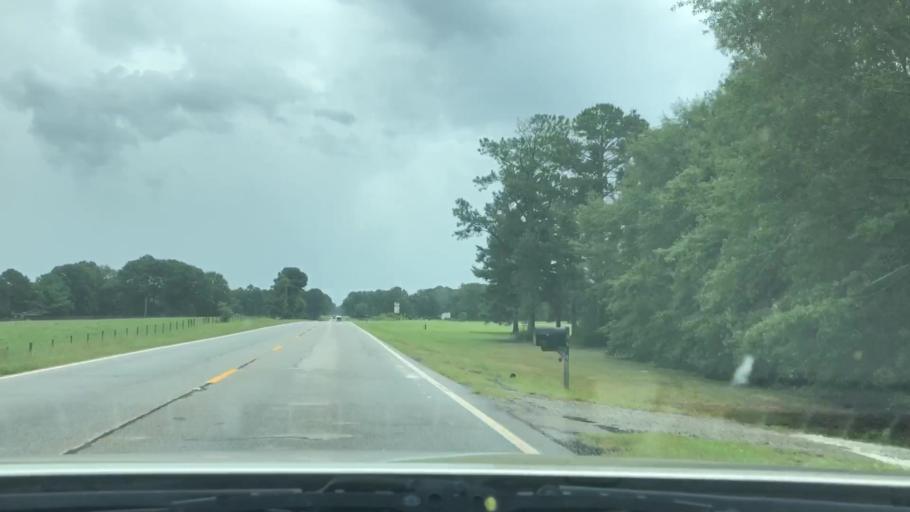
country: US
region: Georgia
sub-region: Pike County
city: Zebulon
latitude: 33.0953
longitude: -84.2840
